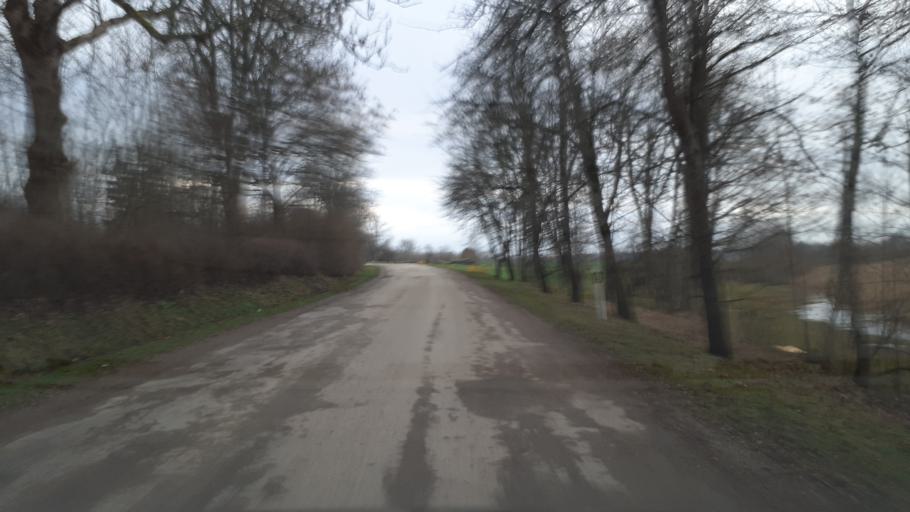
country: LV
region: Aizpute
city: Aizpute
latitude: 56.8016
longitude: 21.6656
